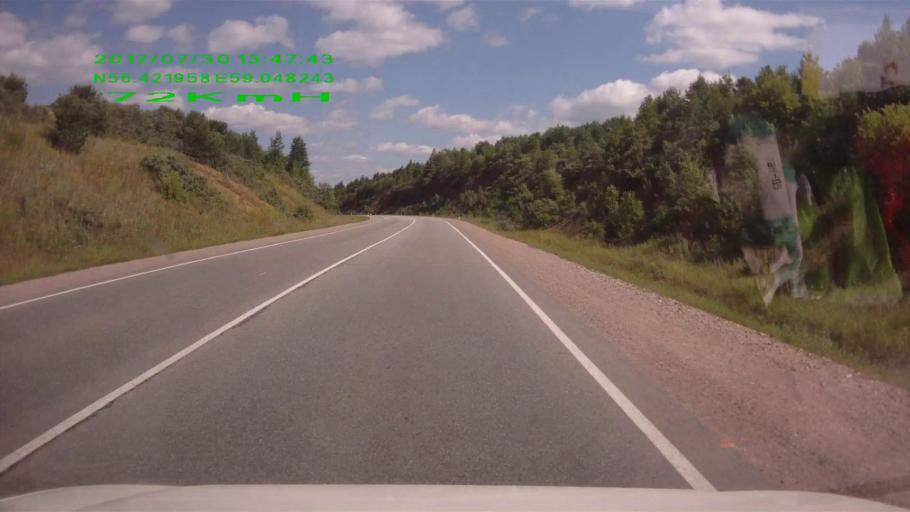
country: RU
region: Sverdlovsk
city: Mikhaylovsk
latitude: 56.4219
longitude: 59.0492
